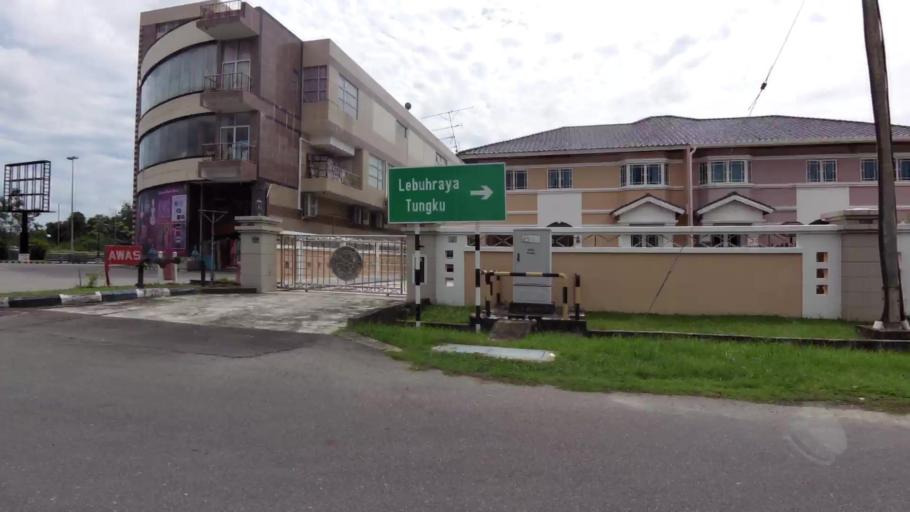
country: BN
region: Brunei and Muara
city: Bandar Seri Begawan
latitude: 4.9167
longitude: 114.9187
